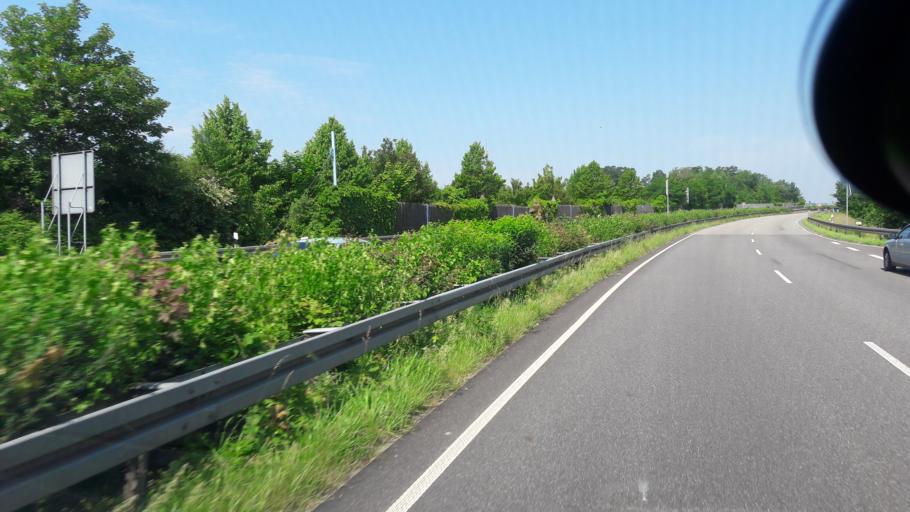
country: DE
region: Baden-Wuerttemberg
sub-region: Karlsruhe Region
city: Bischweier
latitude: 48.8305
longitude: 8.2735
